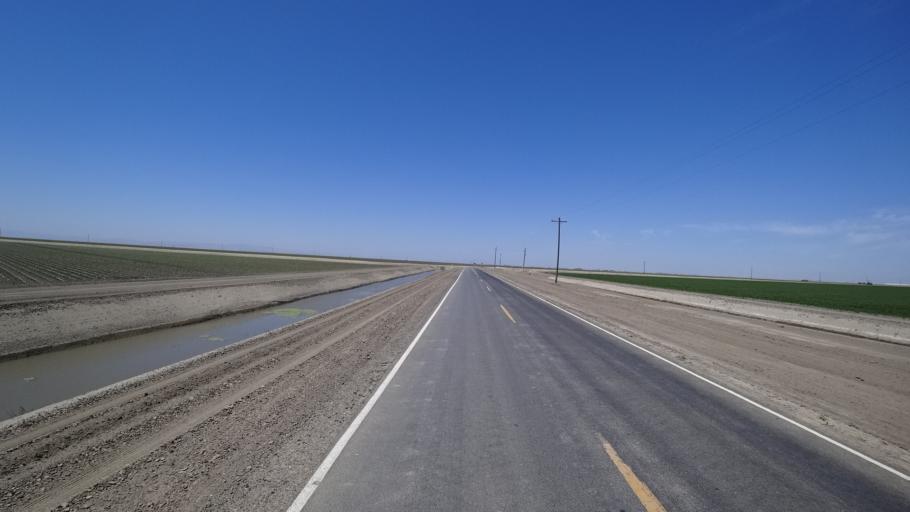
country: US
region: California
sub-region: Kings County
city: Corcoran
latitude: 36.1165
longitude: -119.6782
